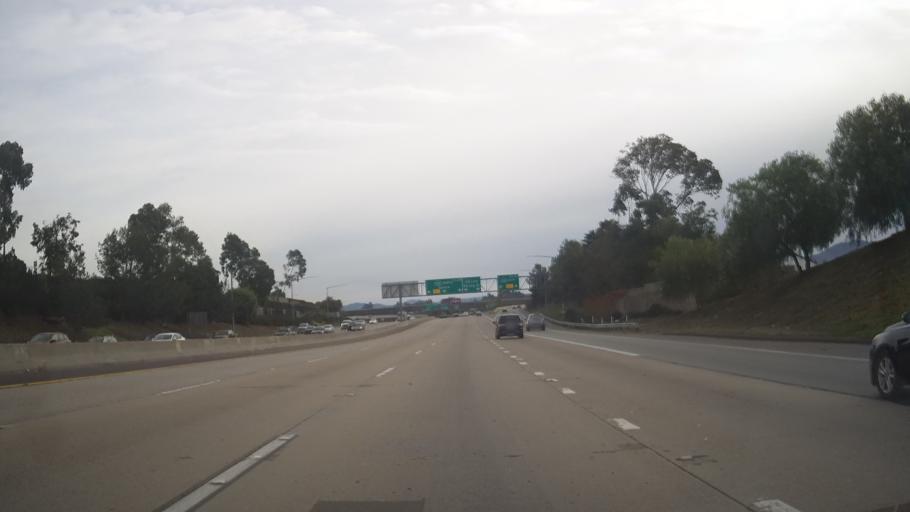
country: US
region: California
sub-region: San Diego County
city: Lemon Grove
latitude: 32.7463
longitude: -117.0249
